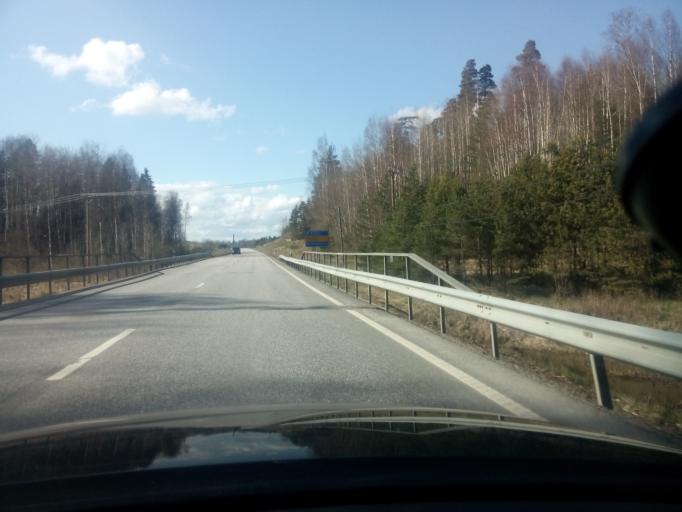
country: SE
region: Soedermanland
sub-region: Flens Kommun
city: Malmkoping
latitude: 59.1180
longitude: 16.7574
